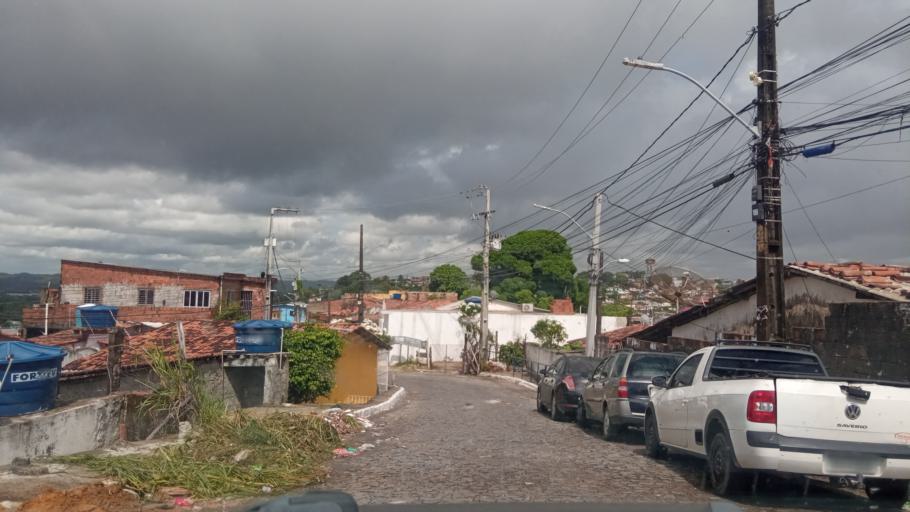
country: BR
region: Pernambuco
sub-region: Jaboatao Dos Guararapes
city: Jaboatao dos Guararapes
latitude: -8.1333
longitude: -34.9542
